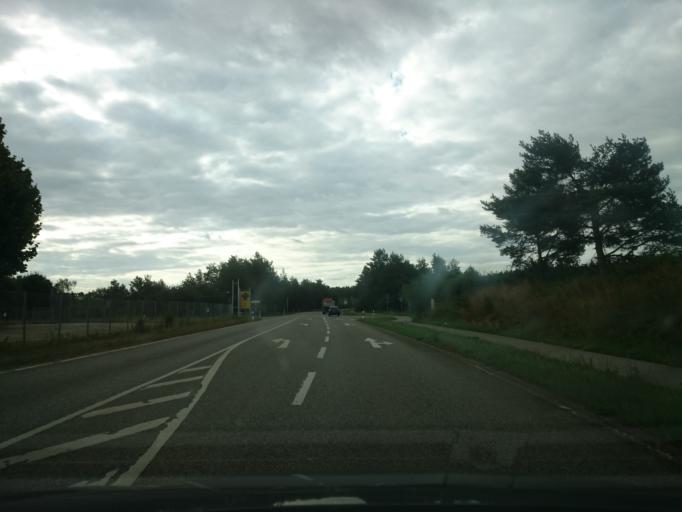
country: DE
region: Bavaria
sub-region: Regierungsbezirk Mittelfranken
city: Hilpoltstein
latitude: 49.1613
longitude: 11.1964
